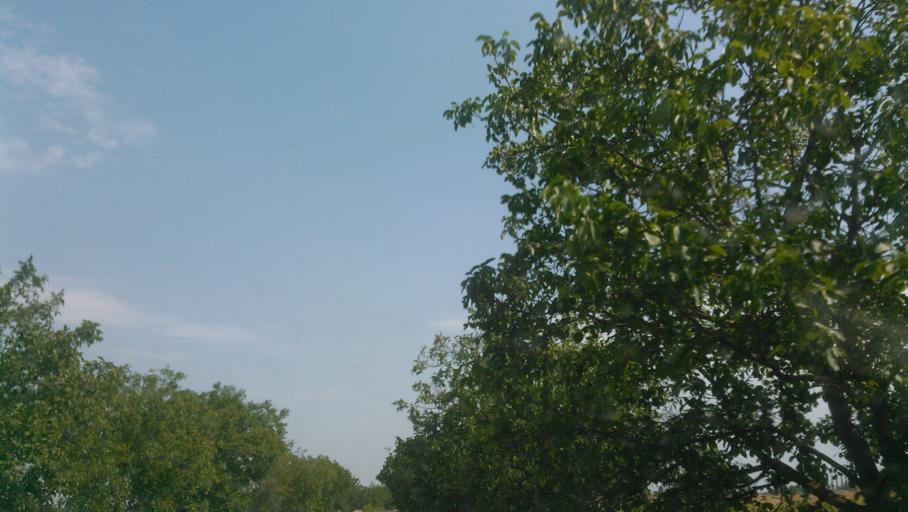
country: SK
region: Trnavsky
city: Dunajska Streda
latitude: 48.0403
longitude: 17.5196
